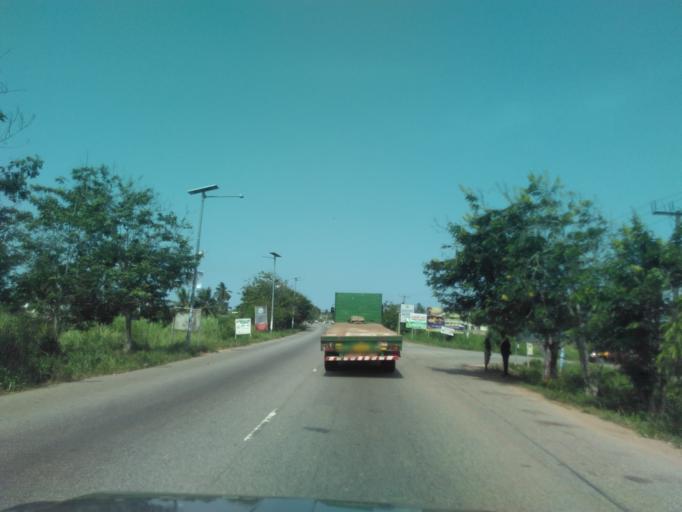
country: GH
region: Central
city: Elmina
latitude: 5.0966
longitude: -1.3353
